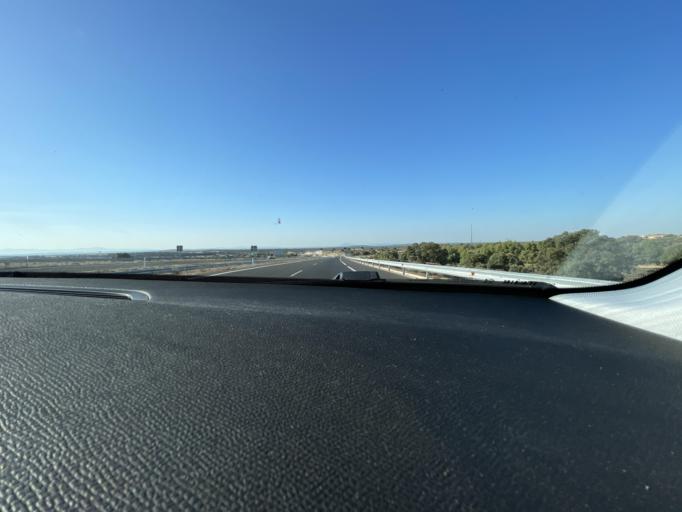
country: ES
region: Castille and Leon
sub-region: Provincia de Salamanca
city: Fuentes de Onoro
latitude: 40.6066
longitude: -6.8140
